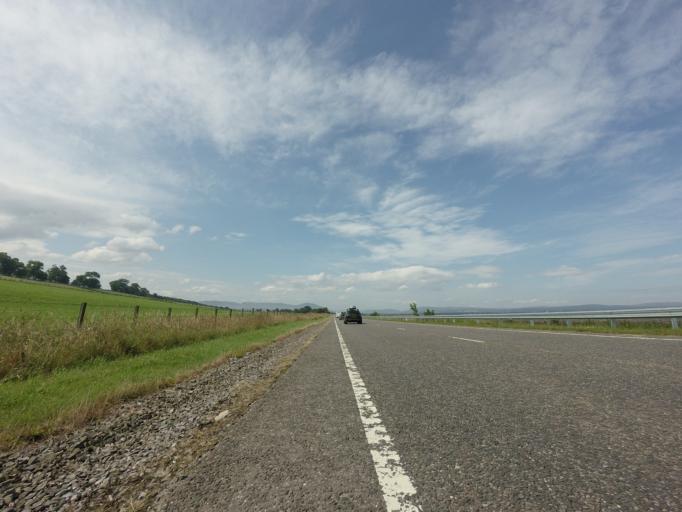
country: GB
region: Scotland
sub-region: Highland
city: Tain
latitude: 57.8297
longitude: -4.0877
